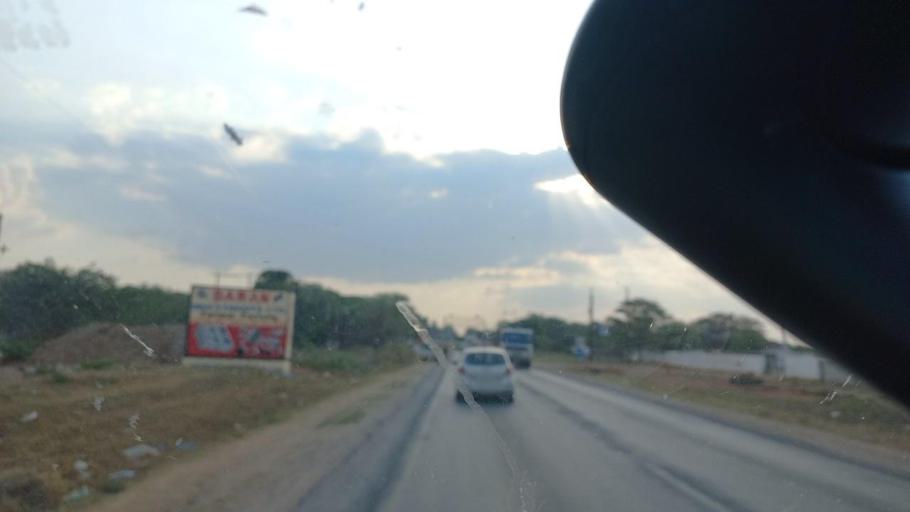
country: ZM
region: Lusaka
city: Lusaka
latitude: -15.3688
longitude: 28.4094
